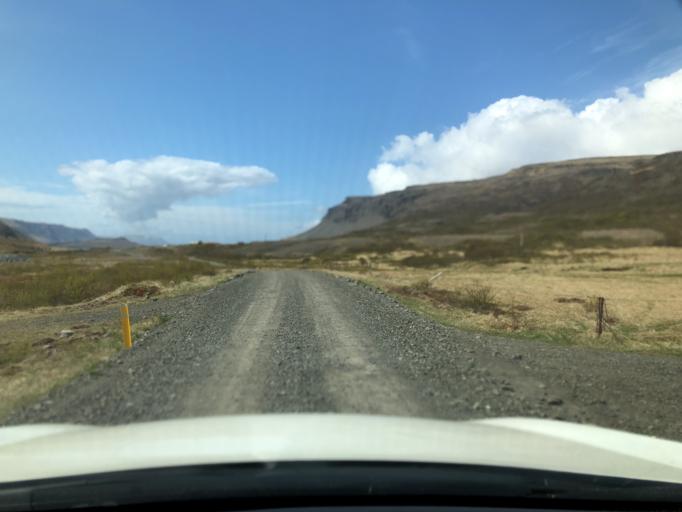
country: IS
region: South
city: Hveragerdi
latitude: 64.3857
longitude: -21.3294
